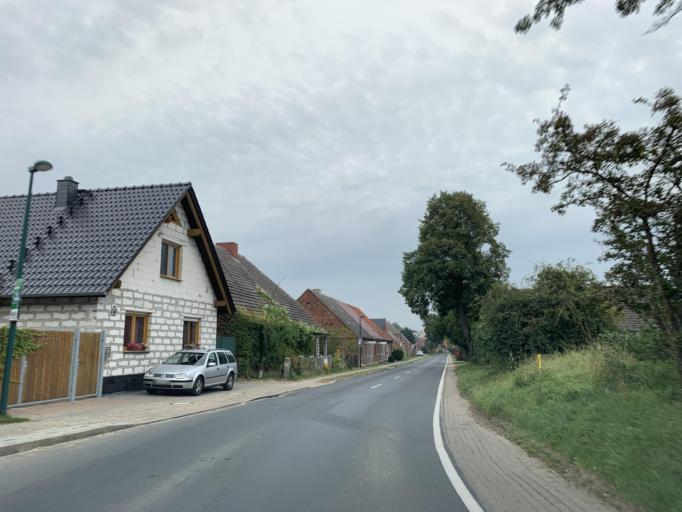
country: DE
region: Brandenburg
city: Mittenwalde
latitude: 53.3274
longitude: 13.7022
